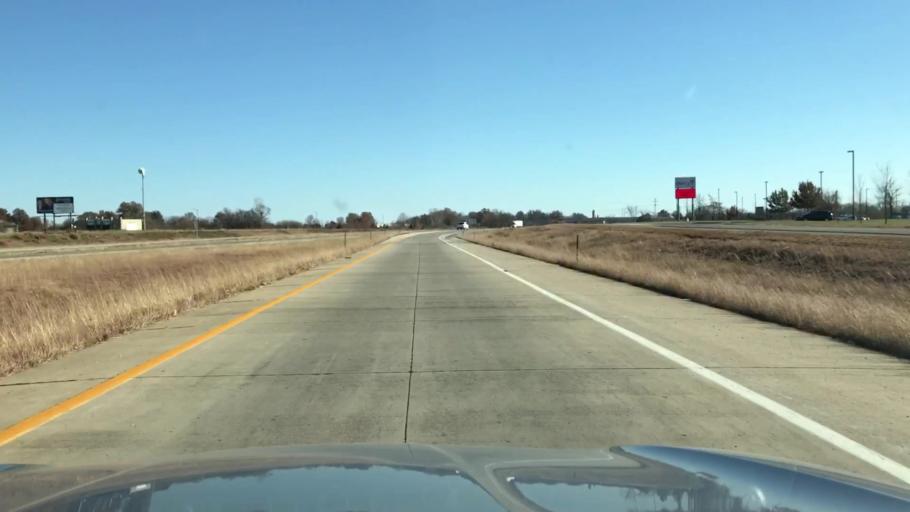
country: US
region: Missouri
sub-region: Jasper County
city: Carthage
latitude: 37.1382
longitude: -94.3214
